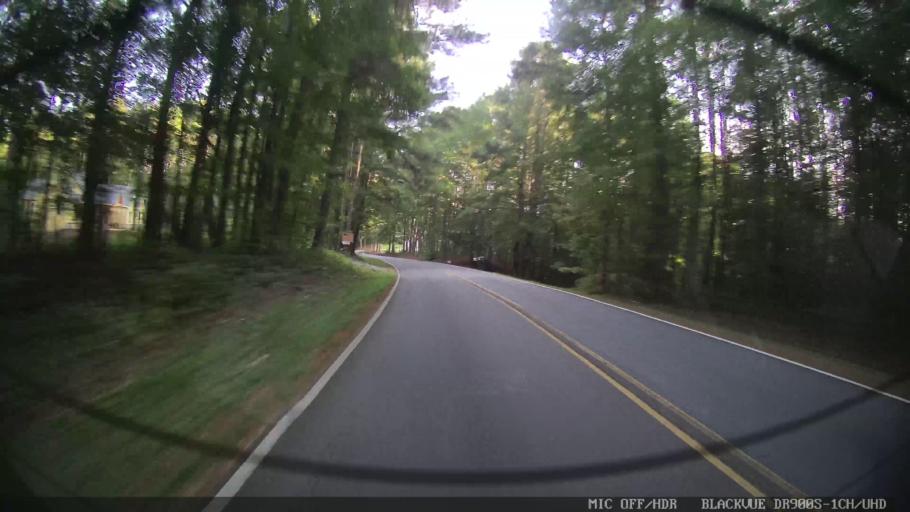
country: US
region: Georgia
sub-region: Bartow County
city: Emerson
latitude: 34.2157
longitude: -84.6948
